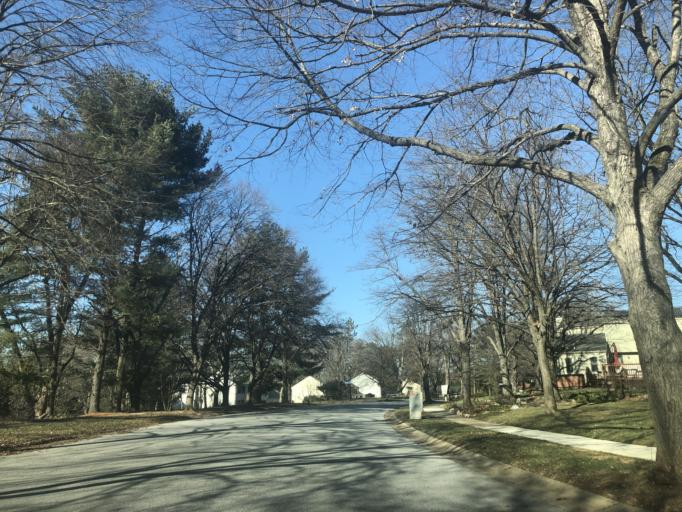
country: US
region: Maryland
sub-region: Howard County
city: Columbia
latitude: 39.1950
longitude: -76.8427
